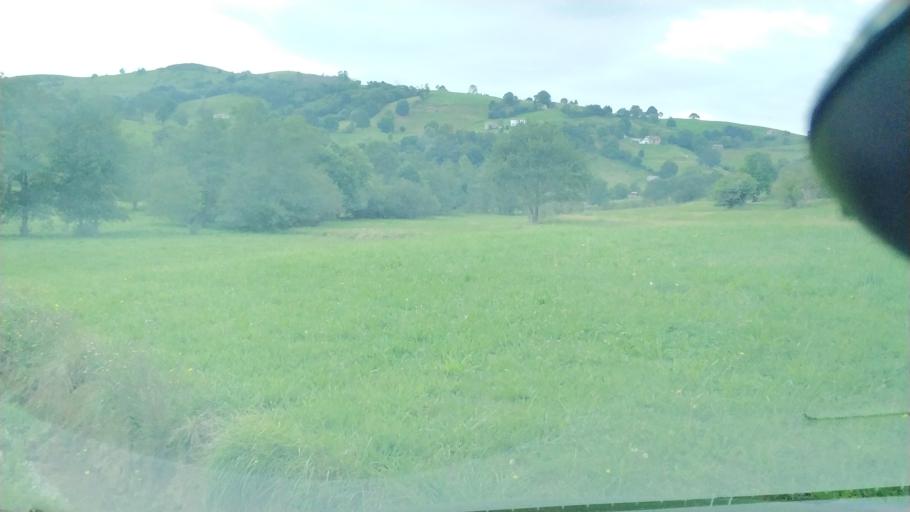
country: ES
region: Cantabria
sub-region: Provincia de Cantabria
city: Santa Maria de Cayon
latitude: 43.2814
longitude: -3.8137
